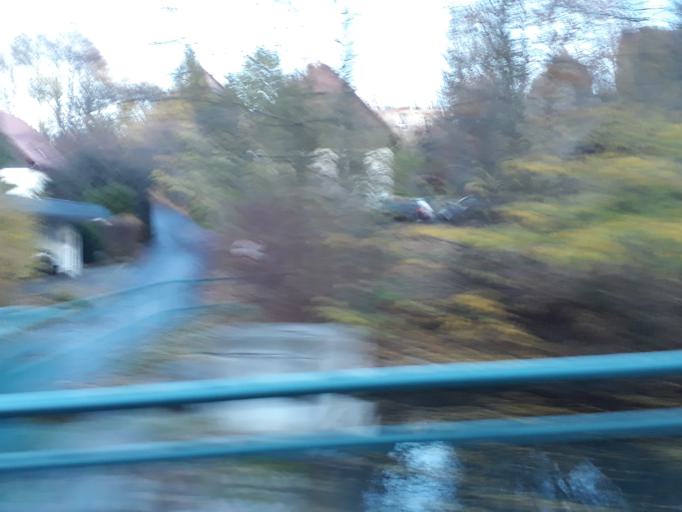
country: DE
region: Saxony
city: Reinhardtsgrimma
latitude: 50.9094
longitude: 13.7882
